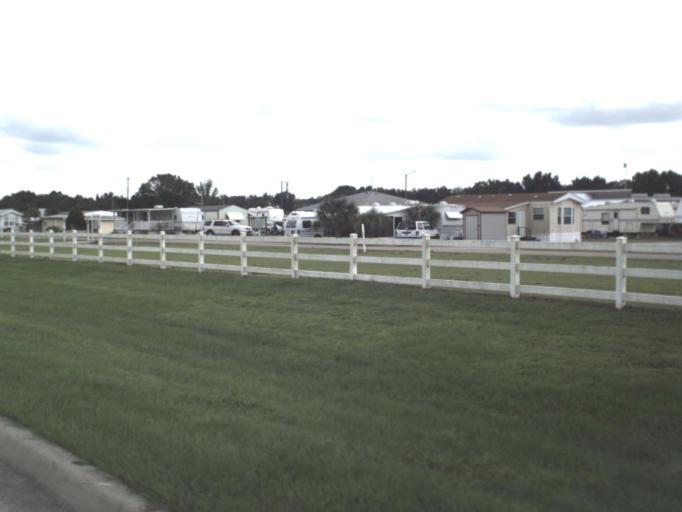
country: US
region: Florida
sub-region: Hardee County
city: Zolfo Springs
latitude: 27.5002
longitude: -81.8006
